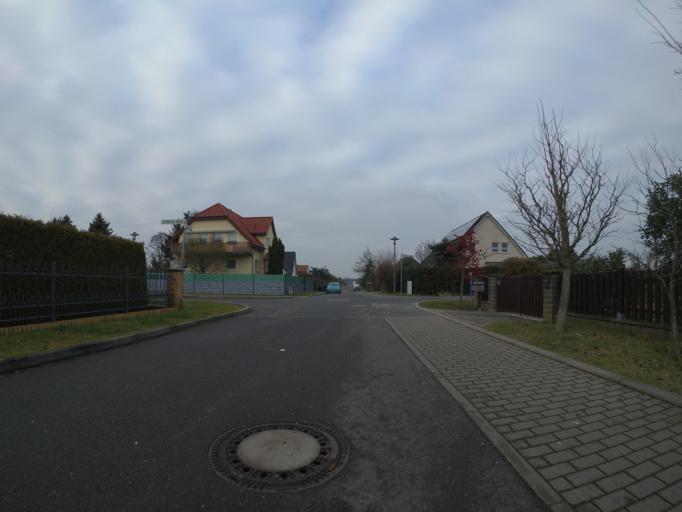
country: DE
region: Brandenburg
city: Ahrensfelde
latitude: 52.5702
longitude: 13.5952
